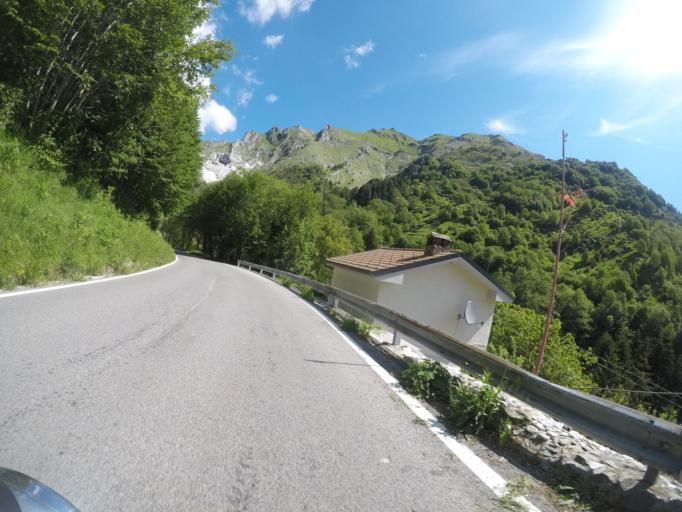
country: IT
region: Tuscany
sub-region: Provincia di Lucca
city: Fontana delle Monache
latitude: 44.0643
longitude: 10.2491
